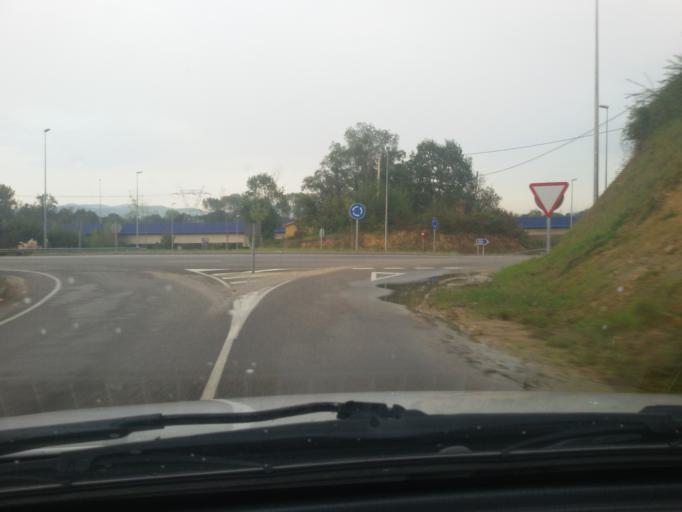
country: ES
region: Asturias
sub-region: Province of Asturias
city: Norena
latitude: 43.3726
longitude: -5.7273
